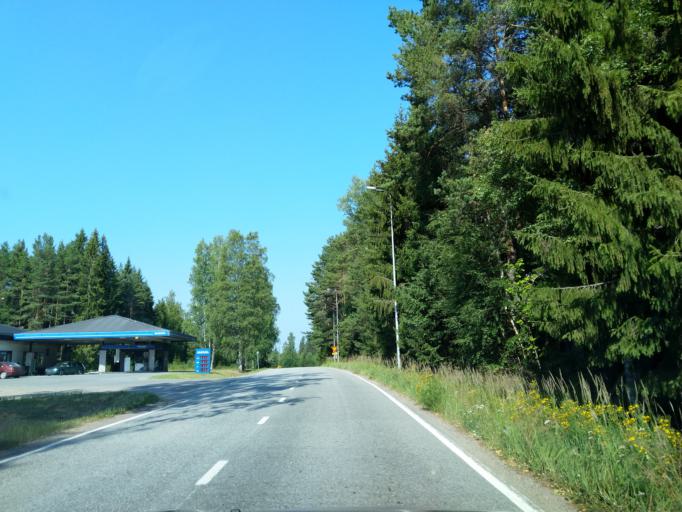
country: FI
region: Satakunta
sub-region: Pori
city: Pomarkku
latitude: 61.6896
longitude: 22.0025
